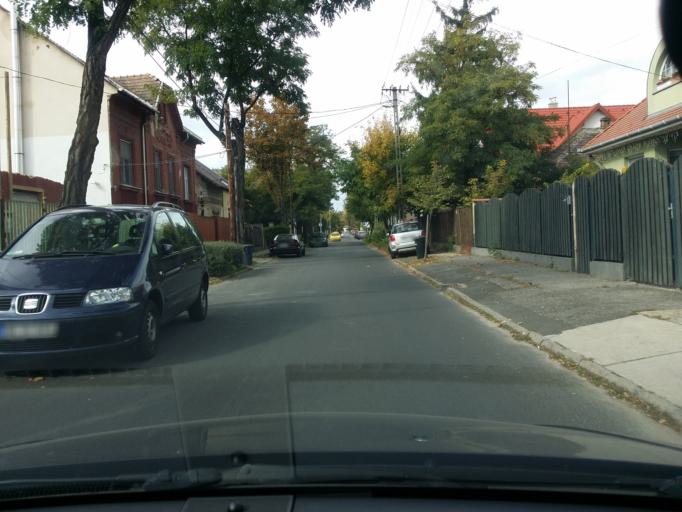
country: HU
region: Budapest
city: Budapest XIV. keruelet
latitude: 47.5372
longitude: 19.1281
